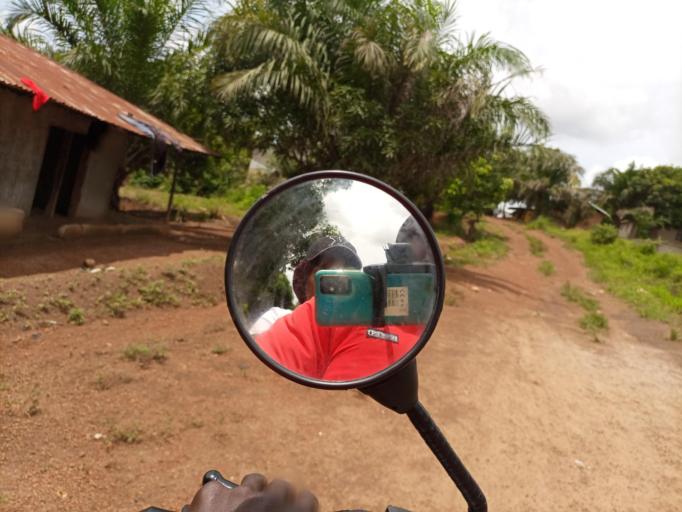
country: SL
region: Southern Province
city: Baoma
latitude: 7.9741
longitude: -11.7125
